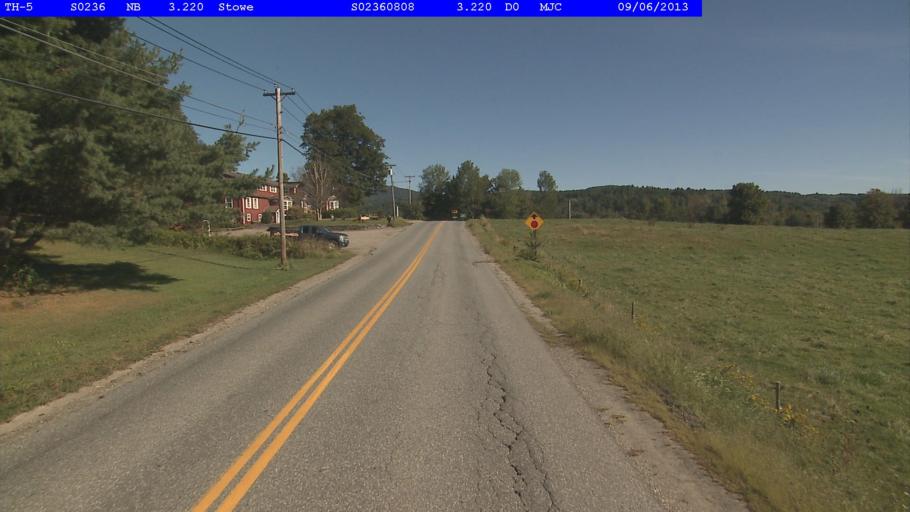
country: US
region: Vermont
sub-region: Lamoille County
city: Morristown
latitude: 44.4709
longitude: -72.7269
